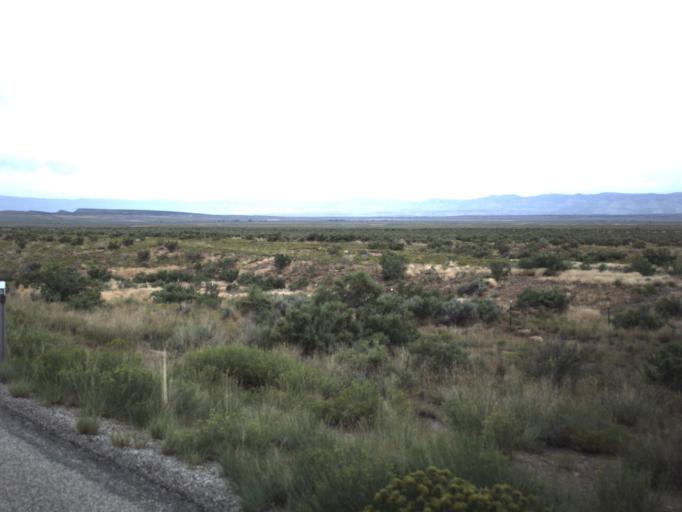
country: US
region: Utah
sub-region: Carbon County
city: East Carbon City
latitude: 39.5347
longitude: -110.5169
